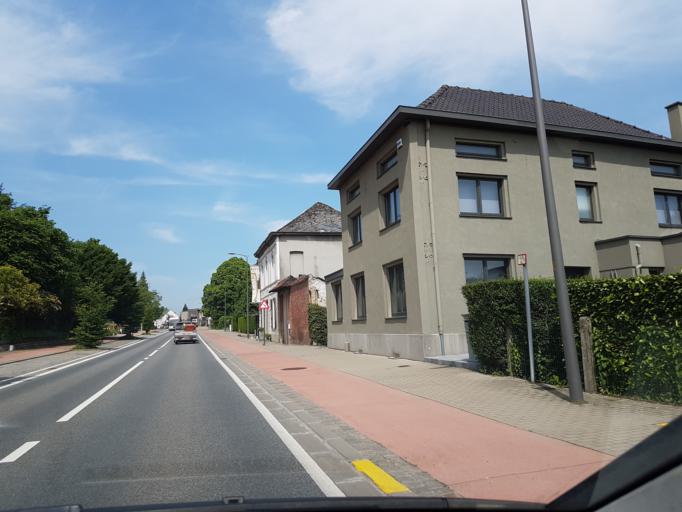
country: BE
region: Flanders
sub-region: Provincie Oost-Vlaanderen
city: Denderleeuw
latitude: 50.9145
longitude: 4.1007
